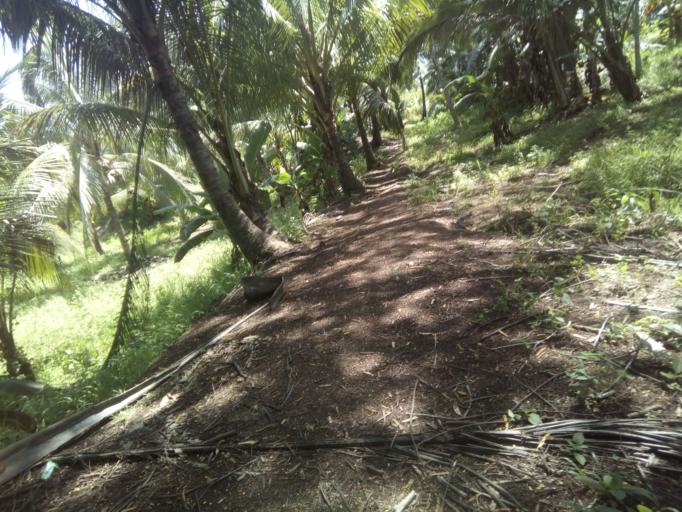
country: PH
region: Caraga
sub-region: Province of Agusan del Sur
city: Santa Josefa
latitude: 7.9579
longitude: 125.9810
